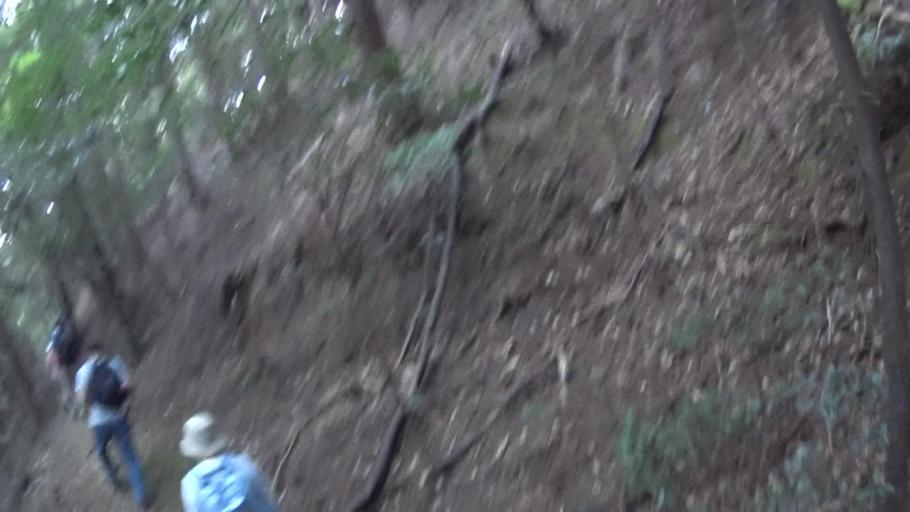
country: JP
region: Osaka
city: Kaizuka
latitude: 34.4835
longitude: 135.3160
